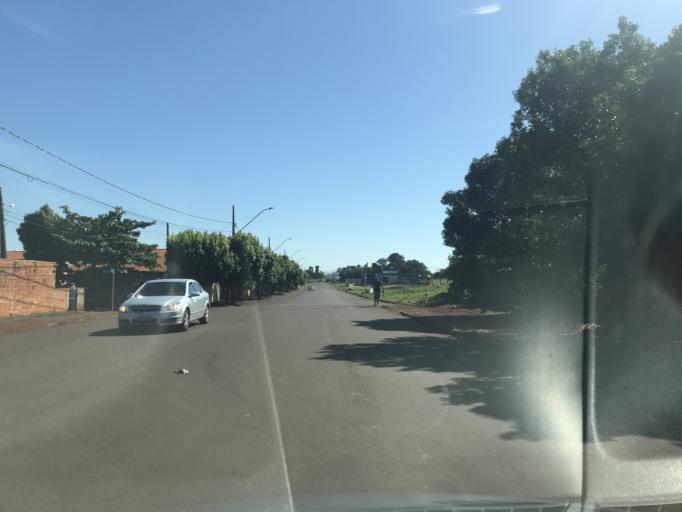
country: BR
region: Parana
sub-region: Palotina
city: Palotina
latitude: -24.2689
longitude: -53.8451
